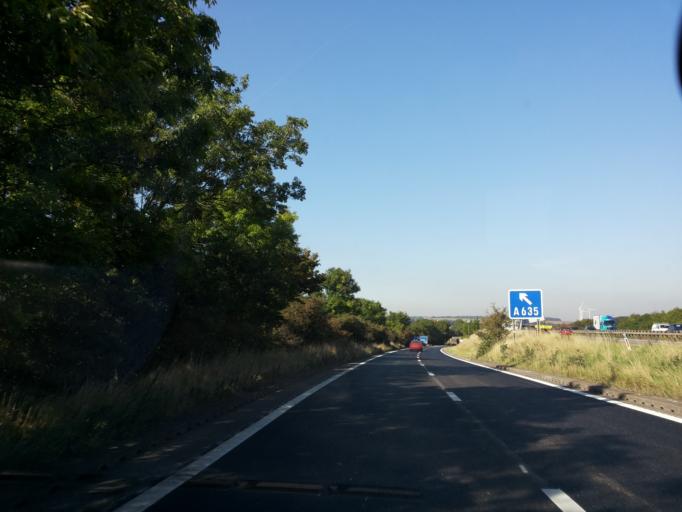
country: GB
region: England
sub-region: Doncaster
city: Marr
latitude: 53.5386
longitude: -1.2031
